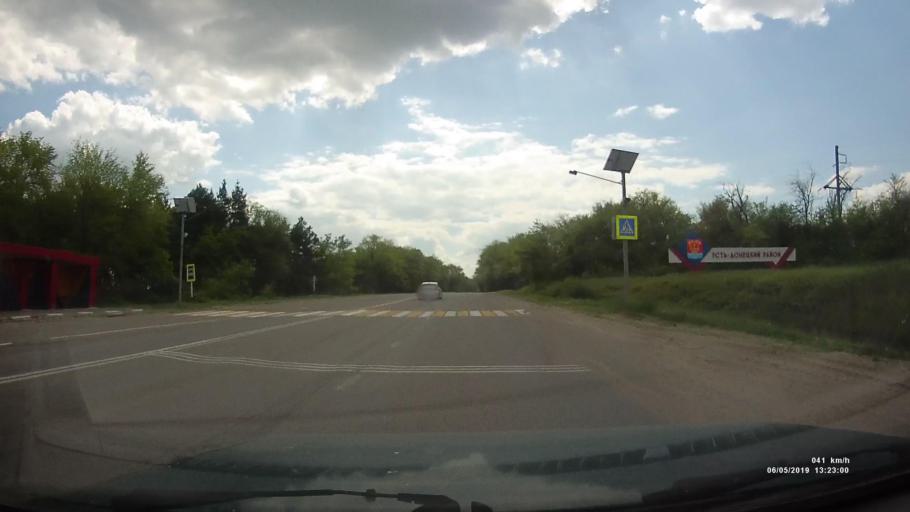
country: RU
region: Rostov
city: Ust'-Donetskiy
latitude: 47.6934
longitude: 40.9226
